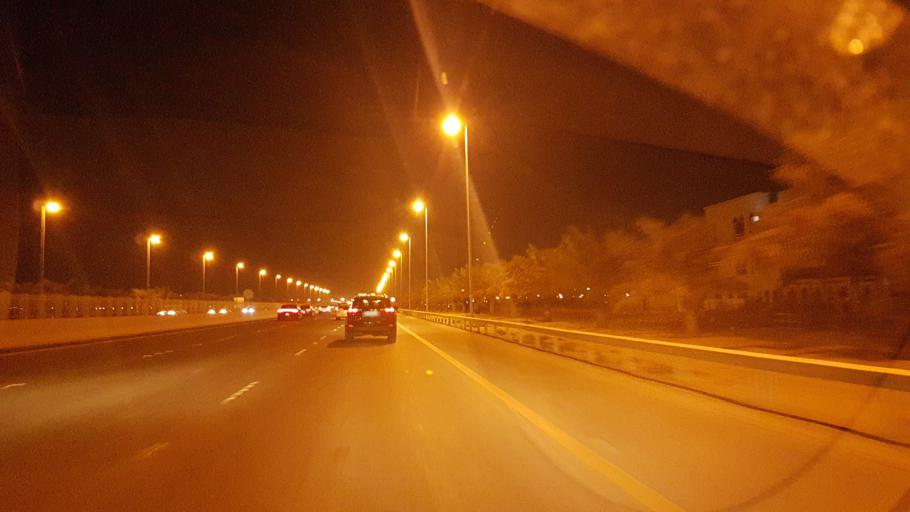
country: BH
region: Muharraq
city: Al Hadd
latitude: 26.2637
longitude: 50.6612
